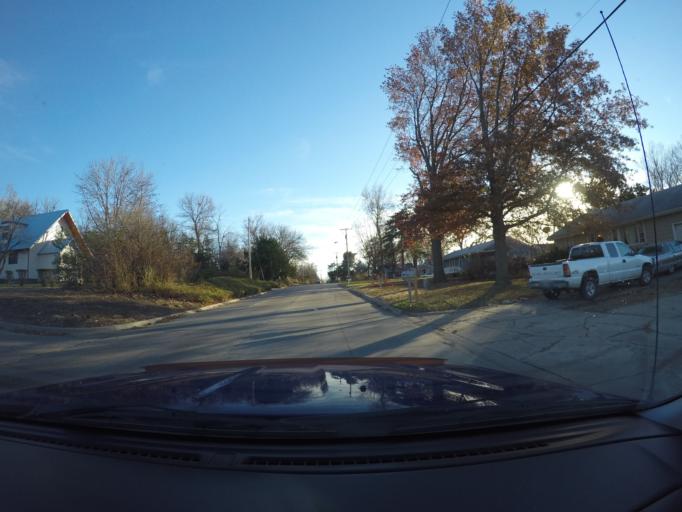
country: US
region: Kansas
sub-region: Riley County
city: Manhattan
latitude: 39.1913
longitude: -96.5982
